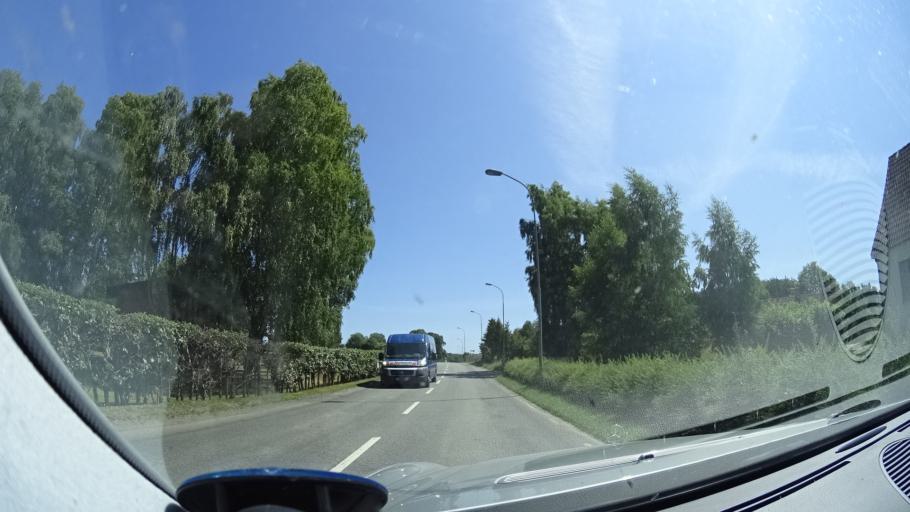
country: SE
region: Skane
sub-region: Kristianstads Kommun
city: Degeberga
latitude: 55.8845
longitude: 14.0190
